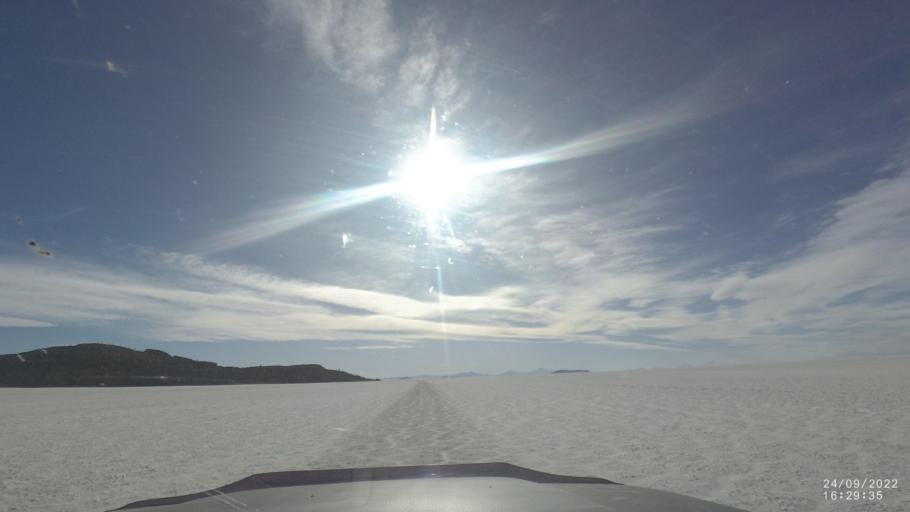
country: BO
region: Potosi
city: Colchani
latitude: -20.2395
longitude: -67.6176
